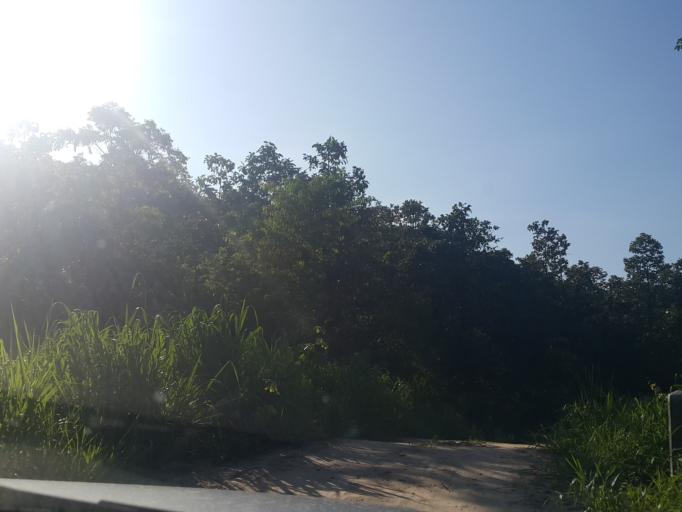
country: TH
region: Chiang Mai
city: Mae On
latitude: 18.7102
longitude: 99.2098
